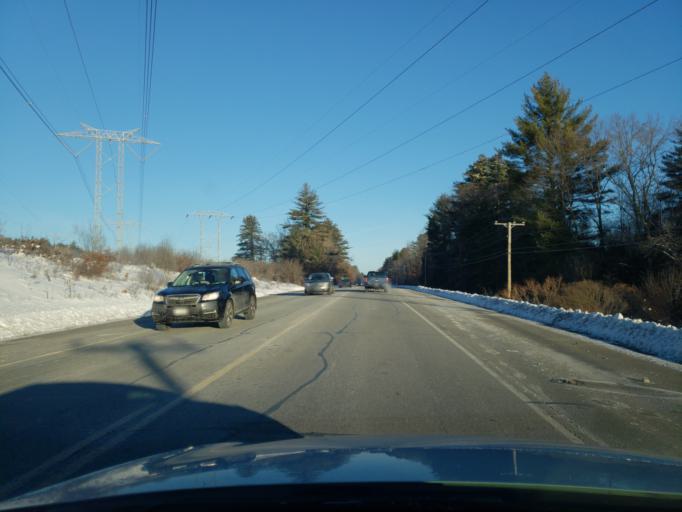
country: US
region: New Hampshire
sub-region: Hillsborough County
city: Pinardville
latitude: 42.9833
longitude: -71.5209
